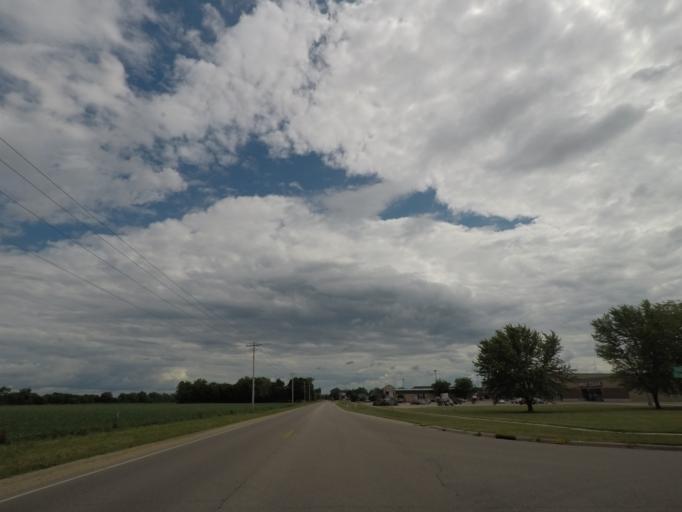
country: US
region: Wisconsin
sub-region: Dane County
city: Belleville
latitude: 42.8765
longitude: -89.5329
